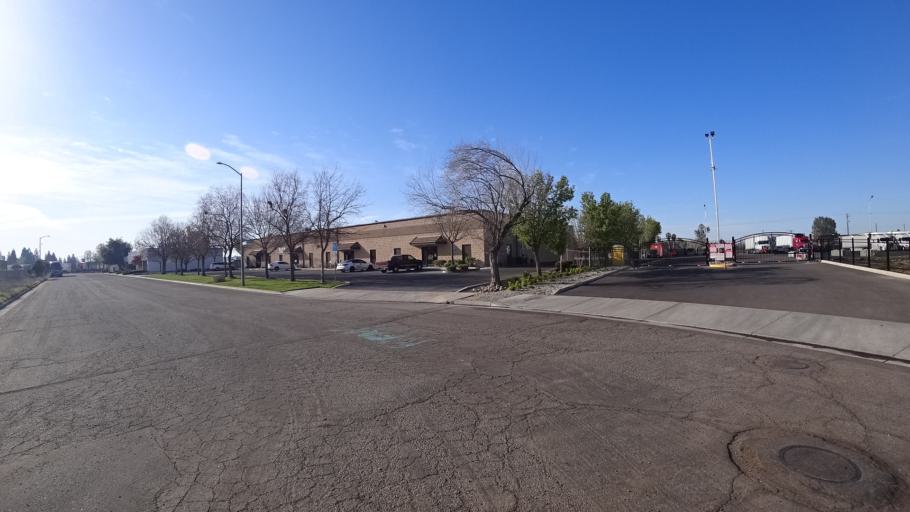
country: US
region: California
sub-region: Fresno County
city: West Park
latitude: 36.8149
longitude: -119.8838
